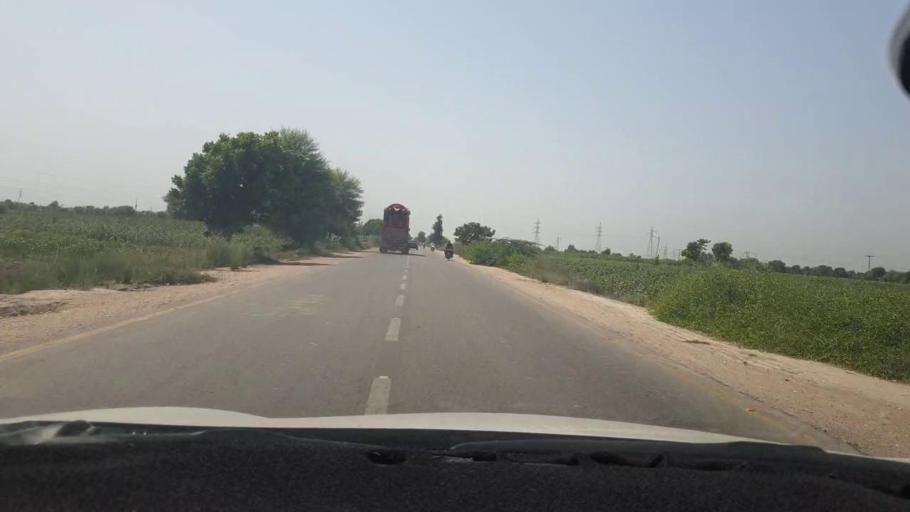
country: PK
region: Sindh
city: Bhit Shah
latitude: 25.8428
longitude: 68.4691
